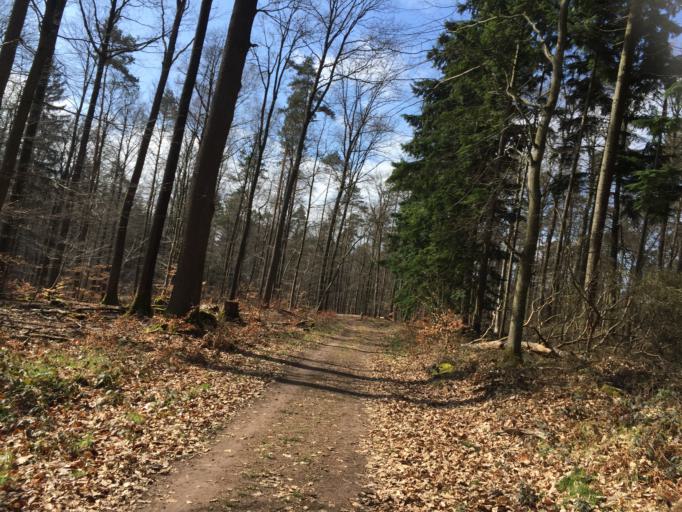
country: DE
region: Rheinland-Pfalz
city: Elmstein
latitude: 49.3894
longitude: 7.9496
